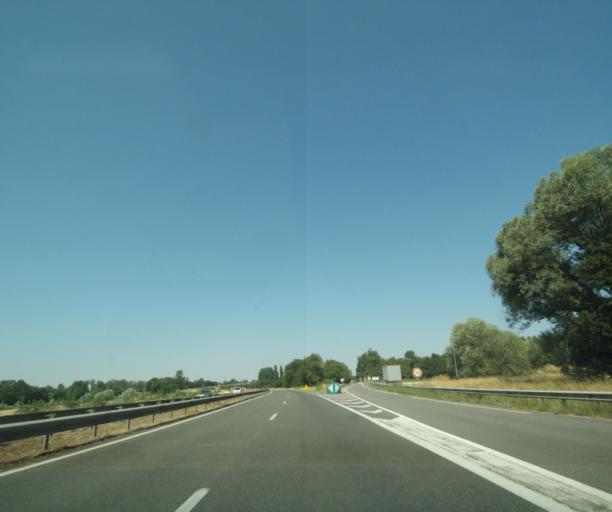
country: FR
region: Champagne-Ardenne
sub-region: Departement de la Haute-Marne
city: Villiers-en-Lieu
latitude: 48.6531
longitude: 4.8347
